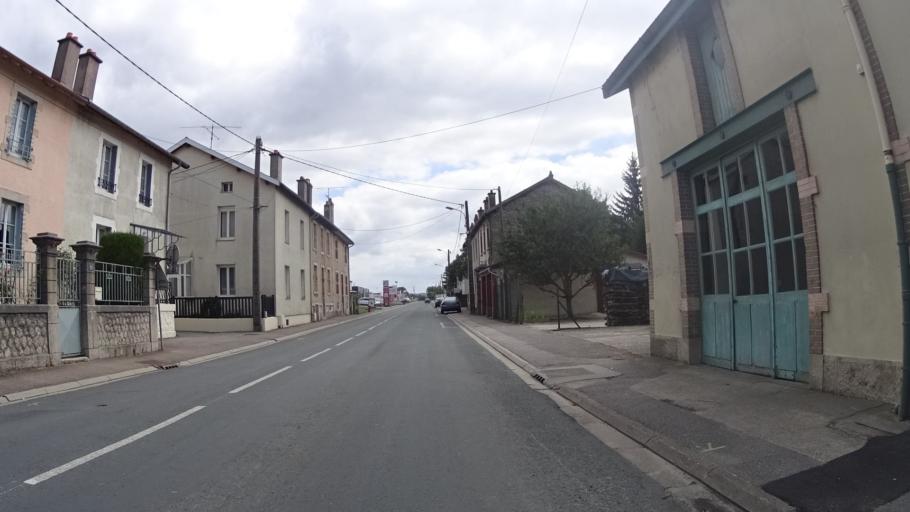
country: FR
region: Lorraine
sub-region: Departement de la Meuse
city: Commercy
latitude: 48.7621
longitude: 5.5993
